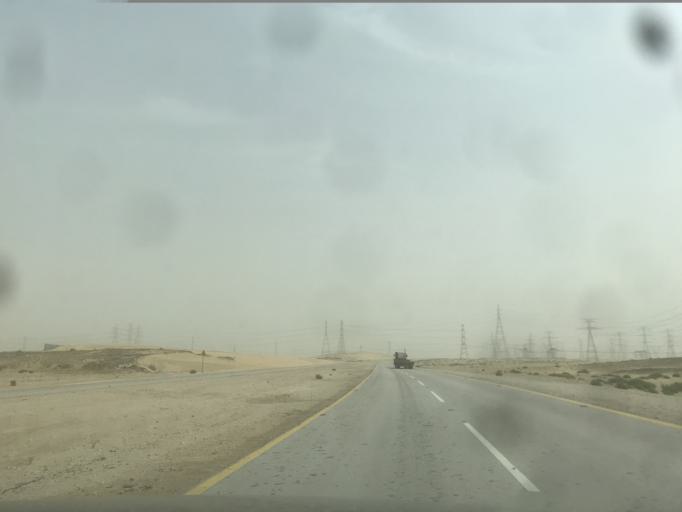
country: SA
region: Eastern Province
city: Abqaiq
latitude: 25.9073
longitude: 49.8935
